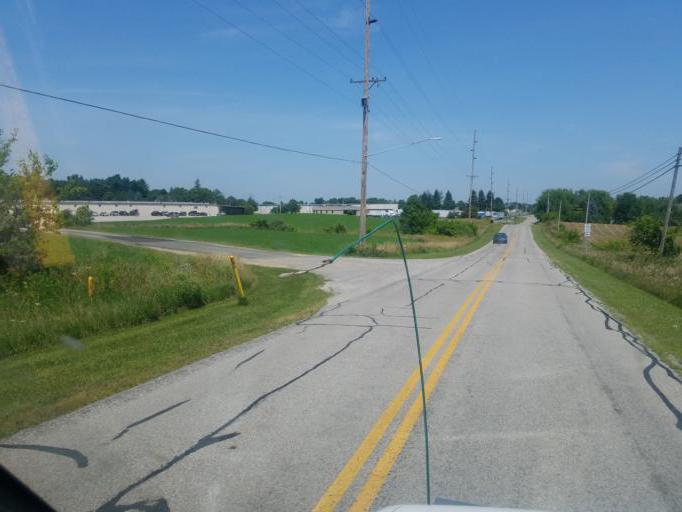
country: US
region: Ohio
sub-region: Logan County
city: West Liberty
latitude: 40.2636
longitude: -83.7593
